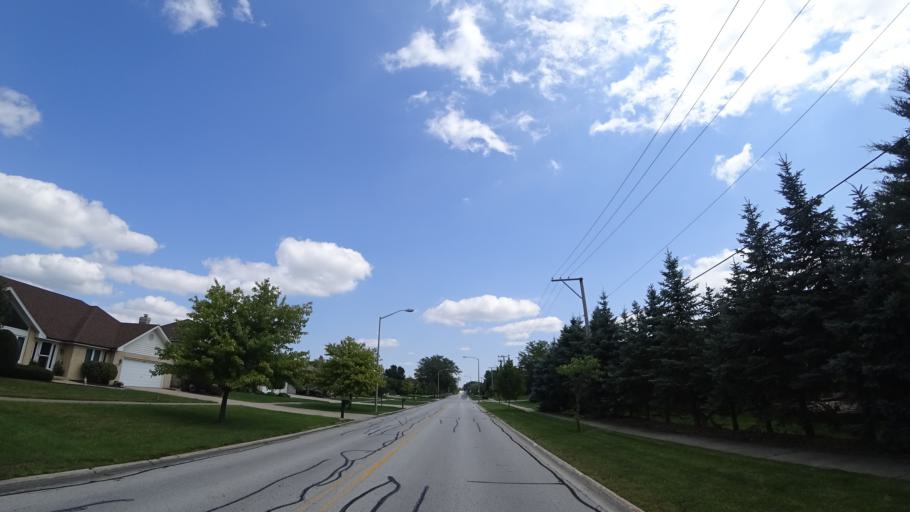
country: US
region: Illinois
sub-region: Cook County
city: Orland Hills
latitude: 41.5724
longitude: -87.8416
